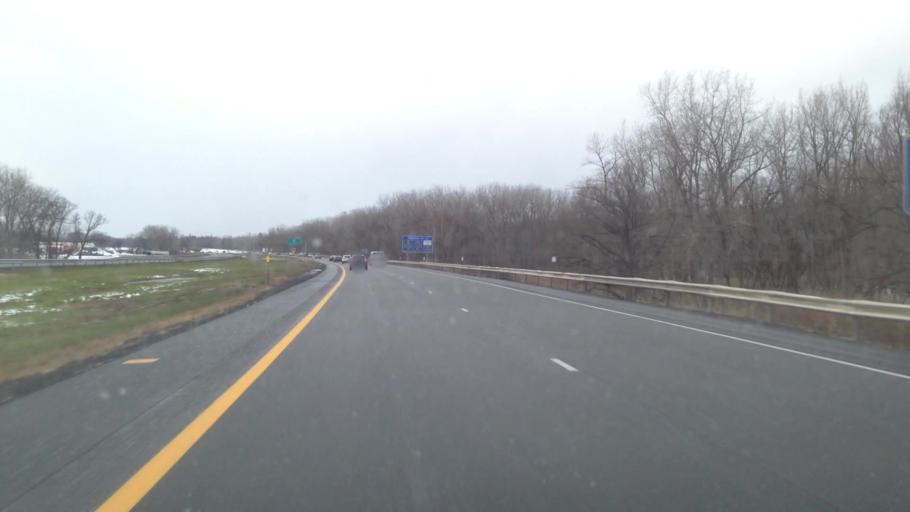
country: US
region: New York
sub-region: Montgomery County
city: Canajoharie
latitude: 42.9030
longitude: -74.5491
